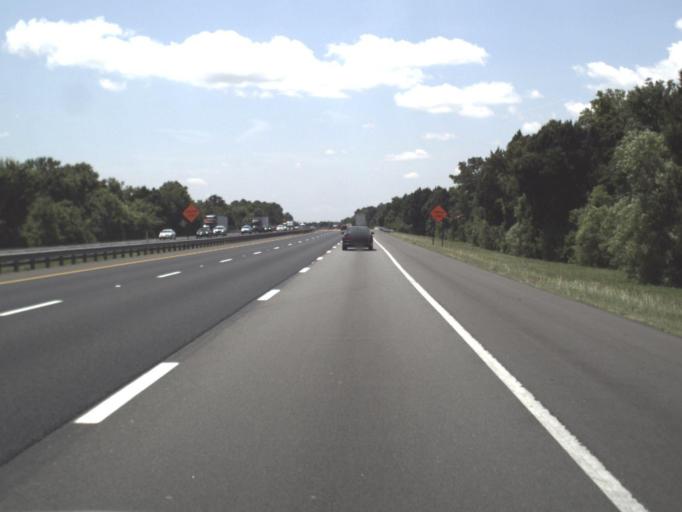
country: US
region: Florida
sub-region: Nassau County
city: Yulee
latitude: 30.5911
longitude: -81.6461
